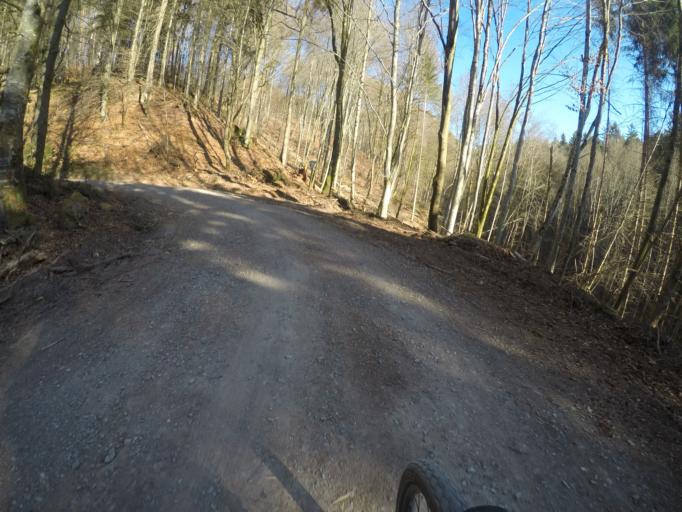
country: DE
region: Baden-Wuerttemberg
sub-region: Regierungsbezirk Stuttgart
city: Waldenbuch
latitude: 48.6064
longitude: 9.1553
